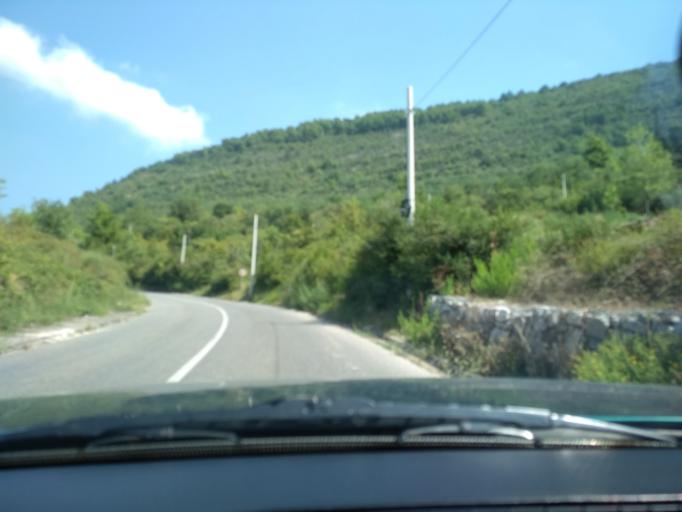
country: ME
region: Kotor
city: Kotor
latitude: 42.3882
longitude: 18.7576
